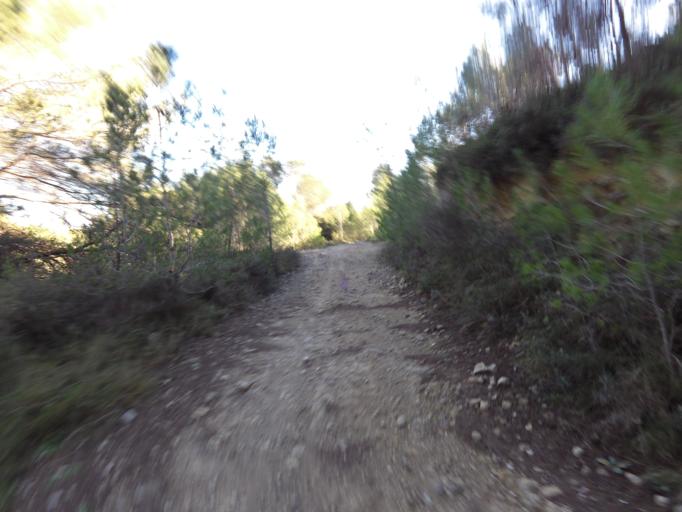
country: FR
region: Languedoc-Roussillon
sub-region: Departement de l'Herault
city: Villetelle
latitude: 43.7345
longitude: 4.1563
